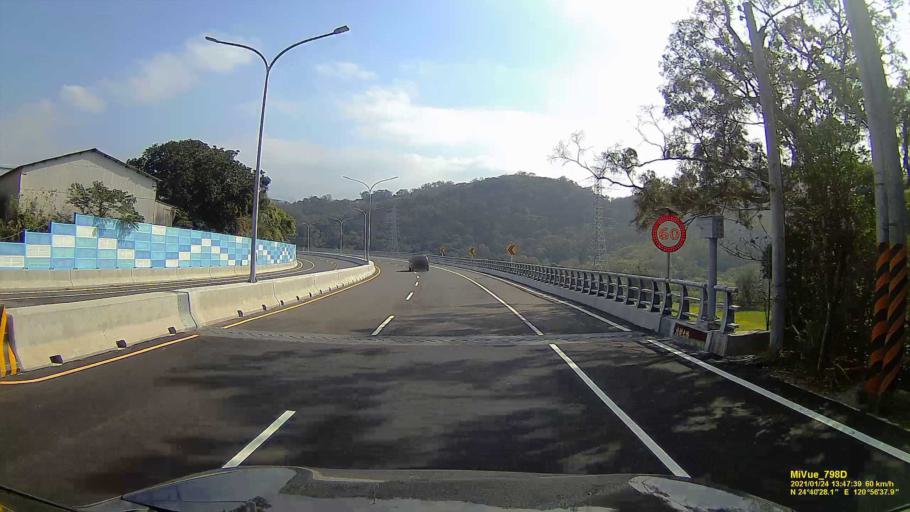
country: TW
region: Taiwan
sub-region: Hsinchu
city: Hsinchu
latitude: 24.6743
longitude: 120.9440
